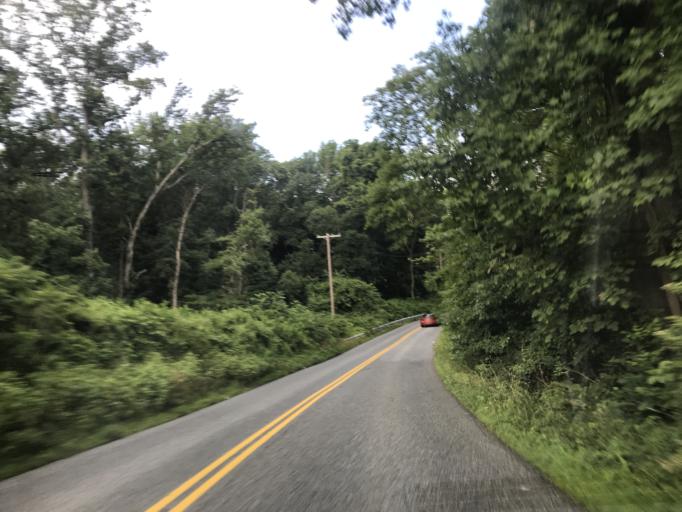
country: US
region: Maryland
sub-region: Harford County
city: Aberdeen
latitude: 39.5160
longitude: -76.2000
